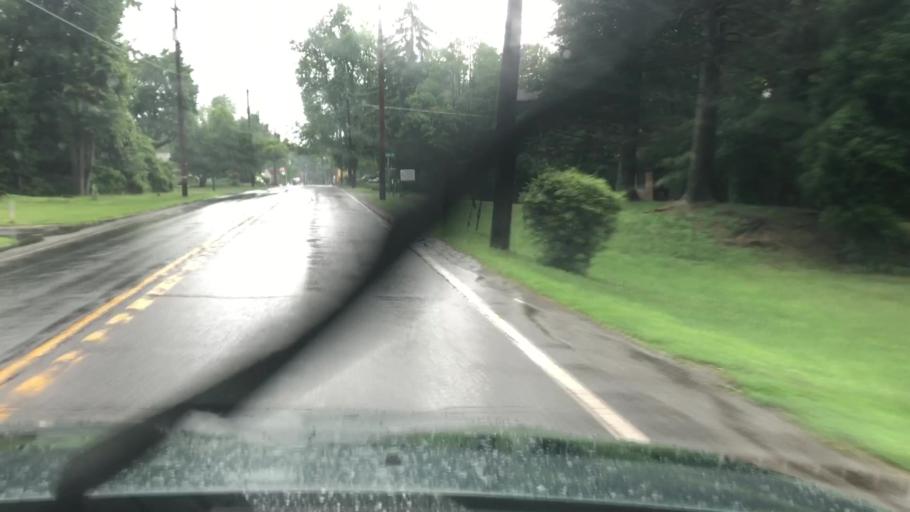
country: US
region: Pennsylvania
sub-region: Monroe County
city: Mountainhome
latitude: 41.1758
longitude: -75.2702
